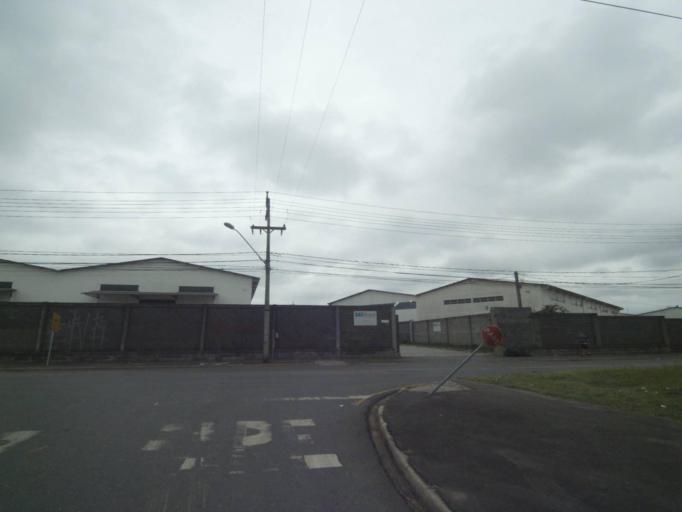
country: BR
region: Parana
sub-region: Araucaria
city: Araucaria
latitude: -25.5414
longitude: -49.3366
